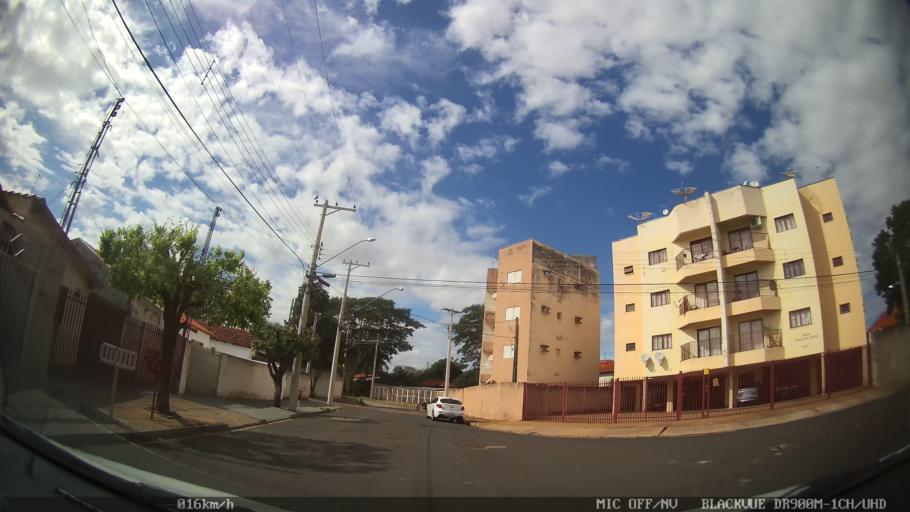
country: BR
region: Sao Paulo
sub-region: Bady Bassitt
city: Bady Bassitt
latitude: -20.8132
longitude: -49.5162
